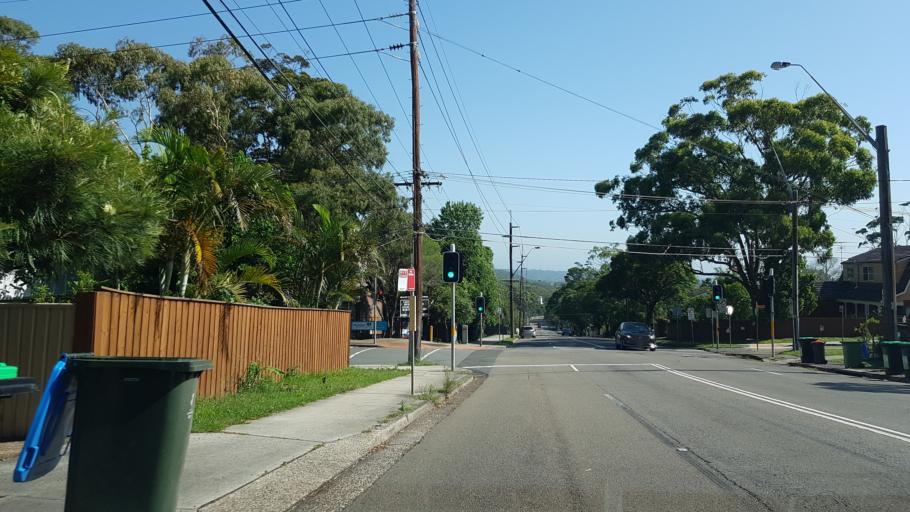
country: AU
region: New South Wales
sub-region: Warringah
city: Narraweena
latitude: -33.7526
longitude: 151.2612
